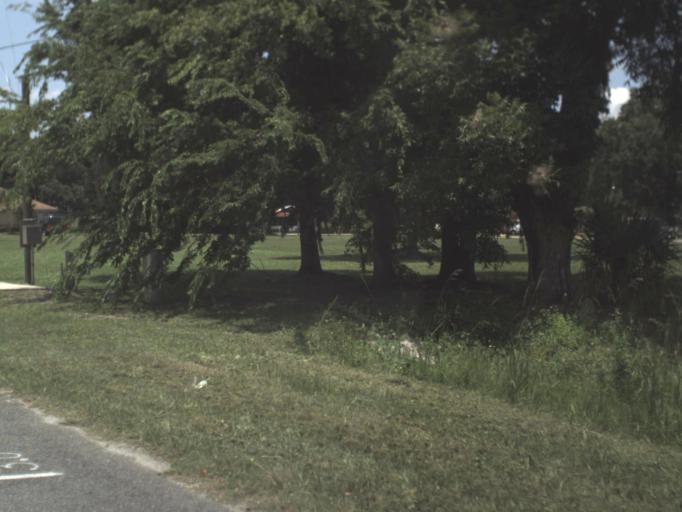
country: US
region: Florida
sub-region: Bradford County
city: Starke
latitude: 29.9496
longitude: -82.0976
